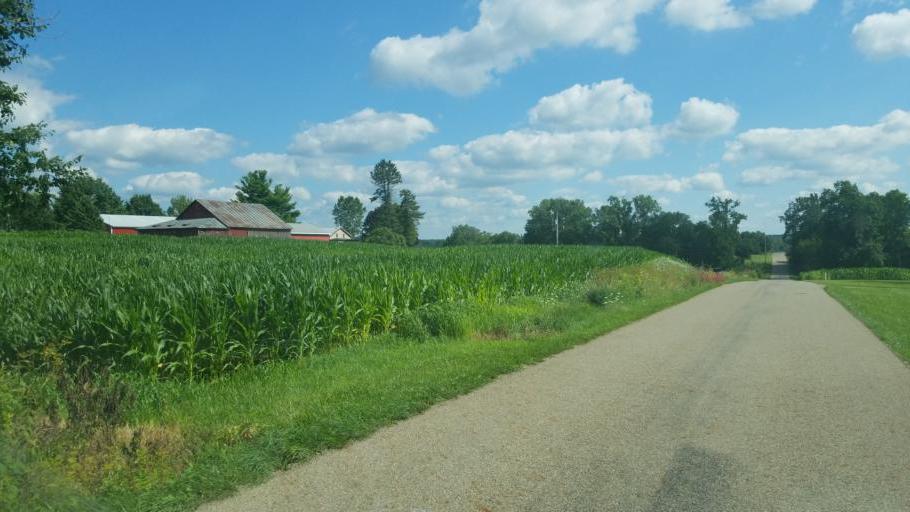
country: US
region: Ohio
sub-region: Knox County
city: Fredericktown
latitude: 40.4727
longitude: -82.6260
